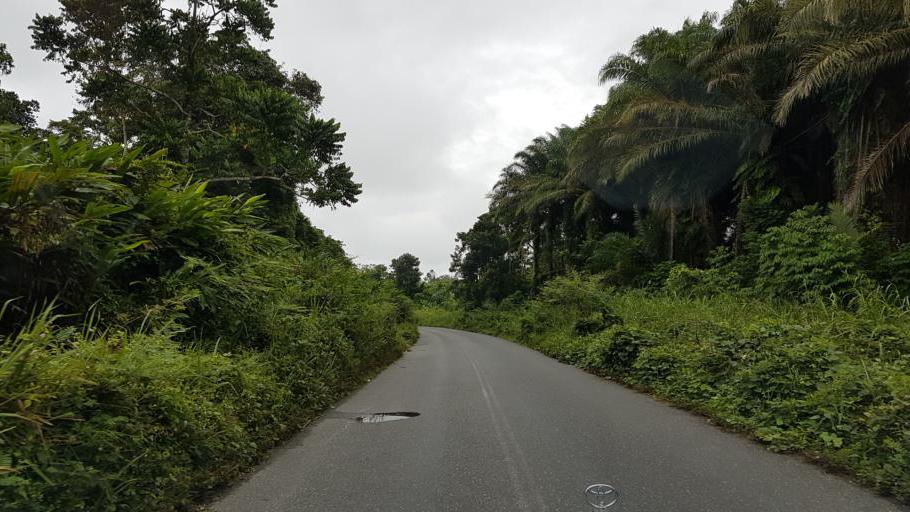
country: PG
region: Northern Province
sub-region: Sohe
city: Popondetta
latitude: -8.8228
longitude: 148.1111
